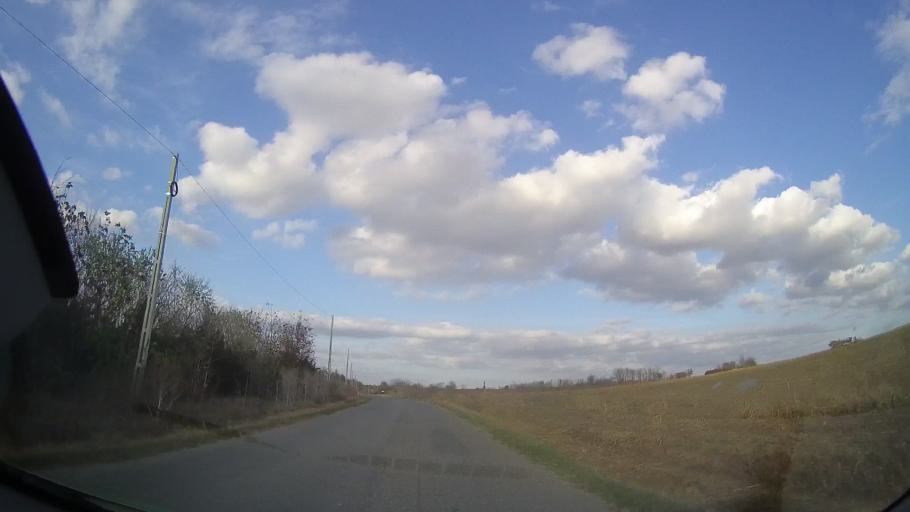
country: RO
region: Constanta
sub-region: Comuna Cerchezu
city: Cerchezu
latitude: 43.8508
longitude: 28.1004
